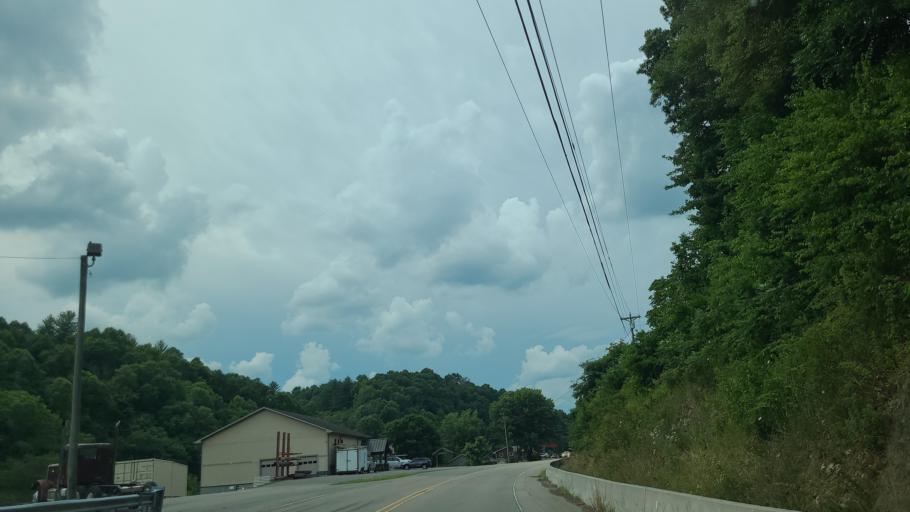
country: US
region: North Carolina
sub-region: Ashe County
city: Jefferson
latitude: 36.3920
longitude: -81.4054
